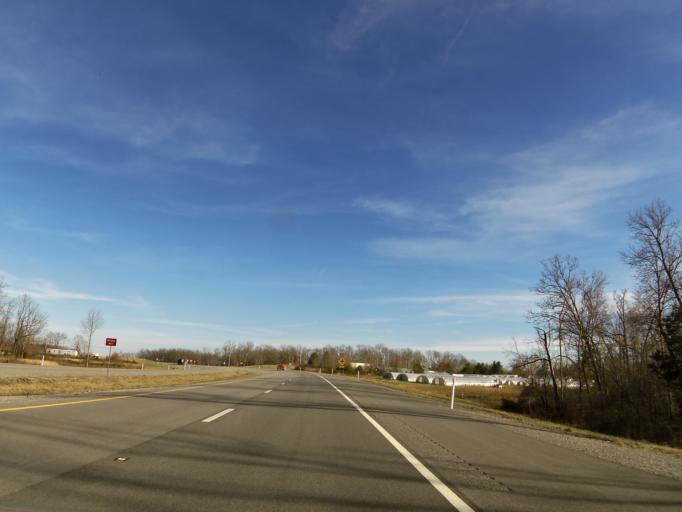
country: US
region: Tennessee
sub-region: Cannon County
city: Woodbury
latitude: 35.7351
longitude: -85.9336
